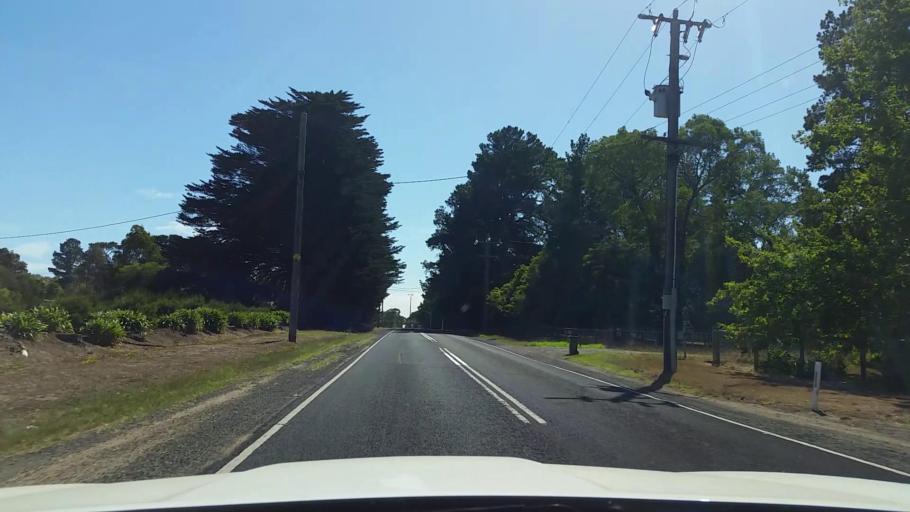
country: AU
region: Victoria
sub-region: Mornington Peninsula
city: Hastings
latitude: -38.2869
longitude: 145.1456
